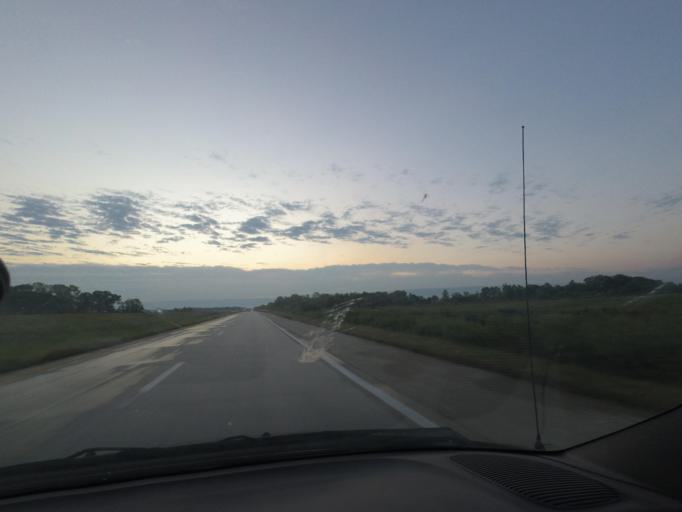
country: US
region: Missouri
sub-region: Macon County
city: Macon
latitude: 39.7602
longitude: -92.6947
